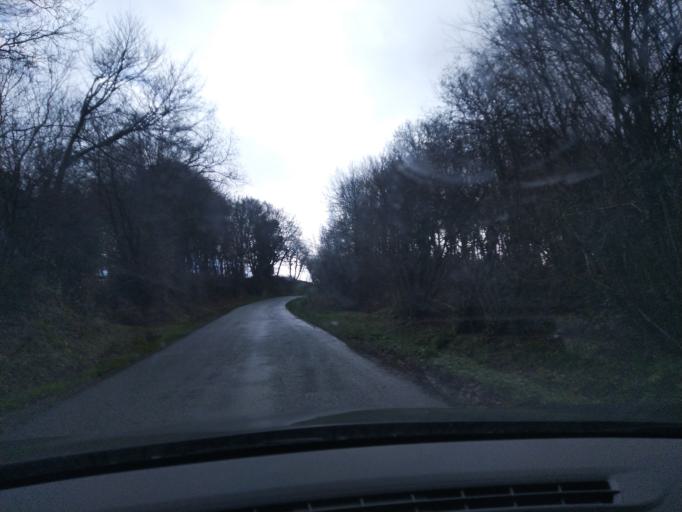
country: FR
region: Brittany
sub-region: Departement du Finistere
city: Guerlesquin
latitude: 48.5007
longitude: -3.5874
